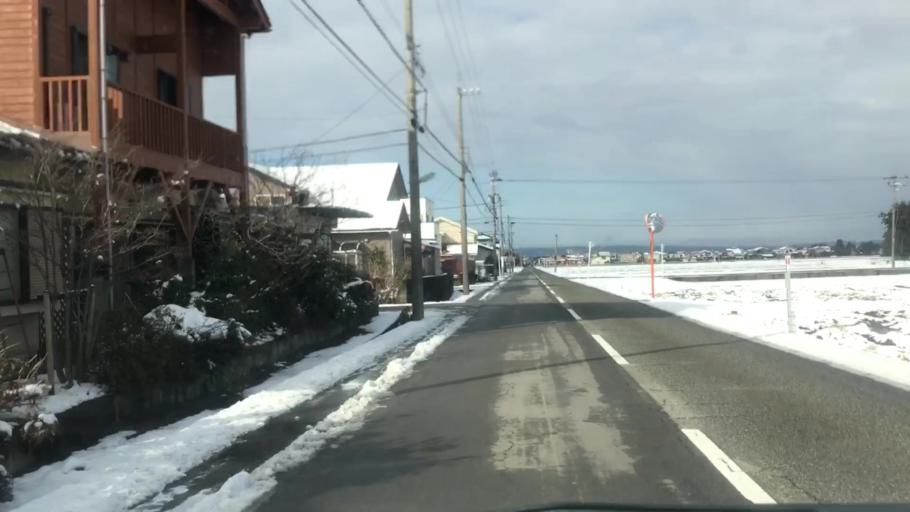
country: JP
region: Toyama
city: Toyama-shi
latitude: 36.6134
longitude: 137.2646
